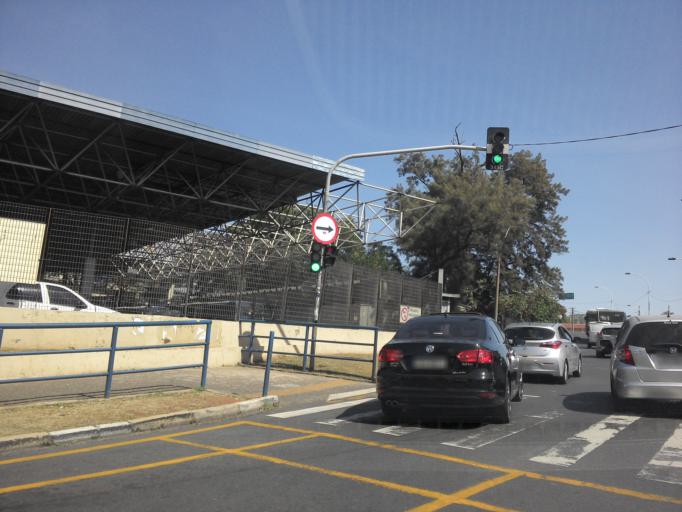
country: BR
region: Sao Paulo
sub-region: Campinas
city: Campinas
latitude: -22.9086
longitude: -47.0627
